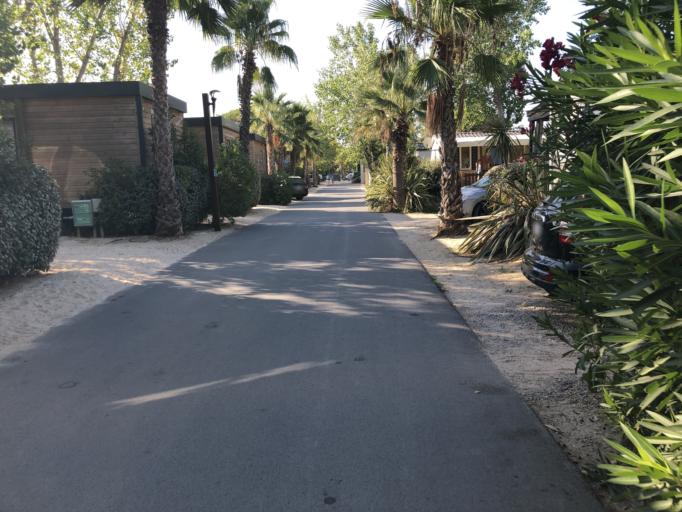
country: FR
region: Provence-Alpes-Cote d'Azur
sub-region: Departement du Var
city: Gassin
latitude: 43.2781
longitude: 6.5811
